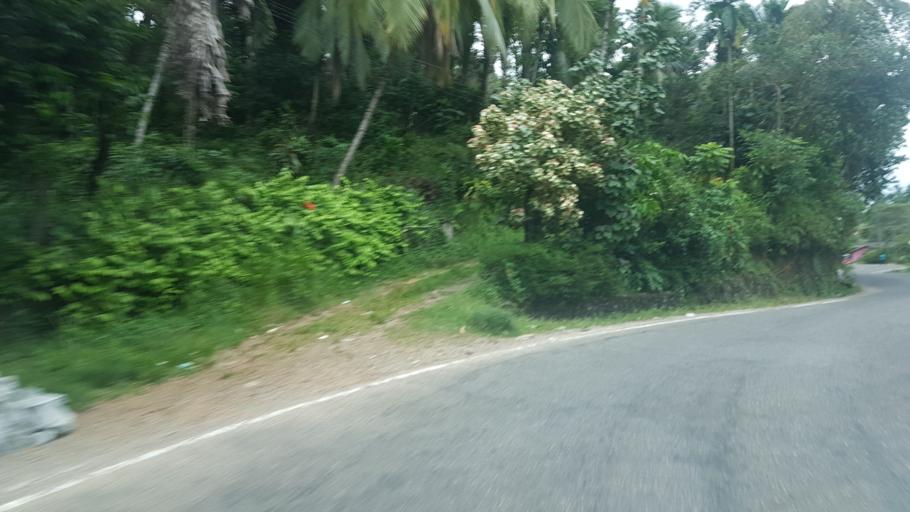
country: LK
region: Western
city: Hanwella Ihala
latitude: 7.0264
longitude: 80.2761
